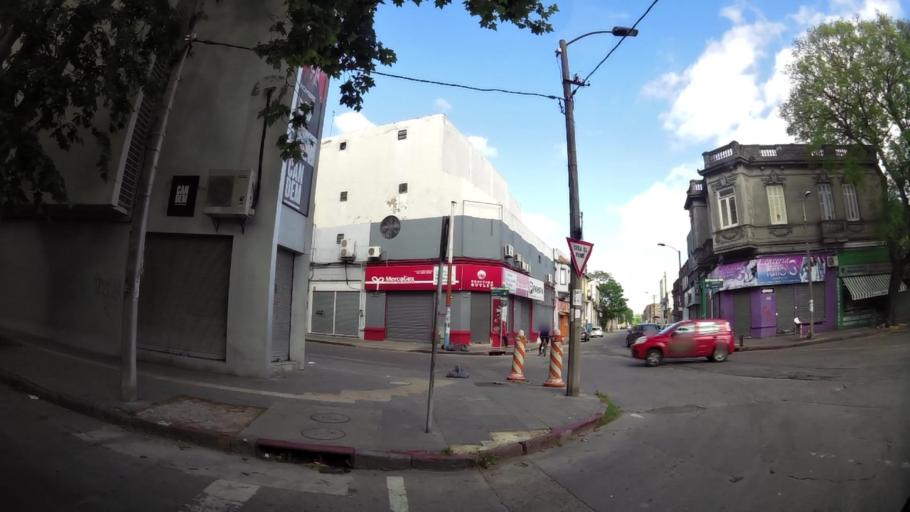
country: UY
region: Montevideo
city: Montevideo
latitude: -34.8874
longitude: -56.1805
